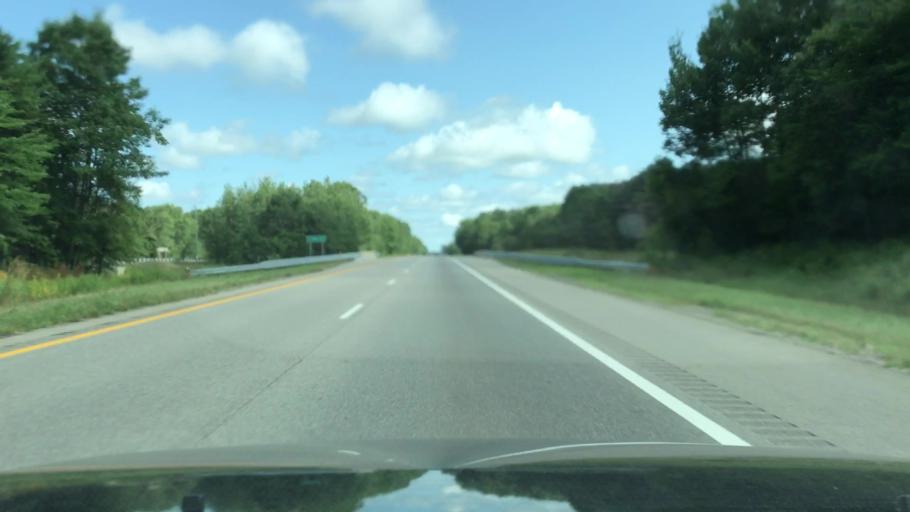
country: US
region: Michigan
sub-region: Montcalm County
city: Howard City
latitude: 43.5104
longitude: -85.4860
